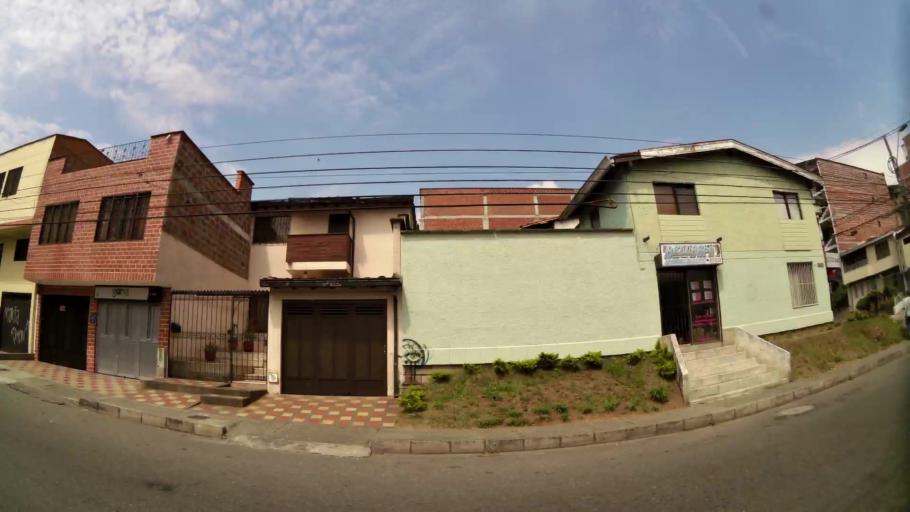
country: CO
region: Antioquia
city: Bello
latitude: 6.3126
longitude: -75.5635
